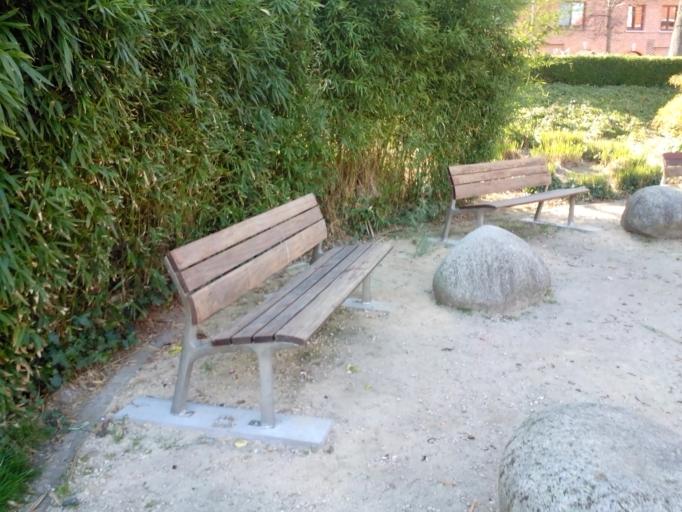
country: BE
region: Flanders
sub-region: Provincie Vlaams-Brabant
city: Leuven
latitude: 50.8749
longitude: 4.6890
